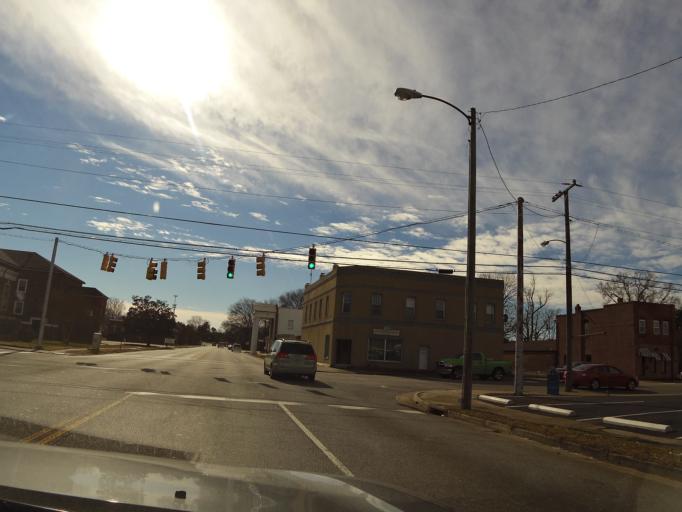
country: US
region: Virginia
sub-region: City of Hopewell
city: Hopewell
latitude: 37.3038
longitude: -77.2930
